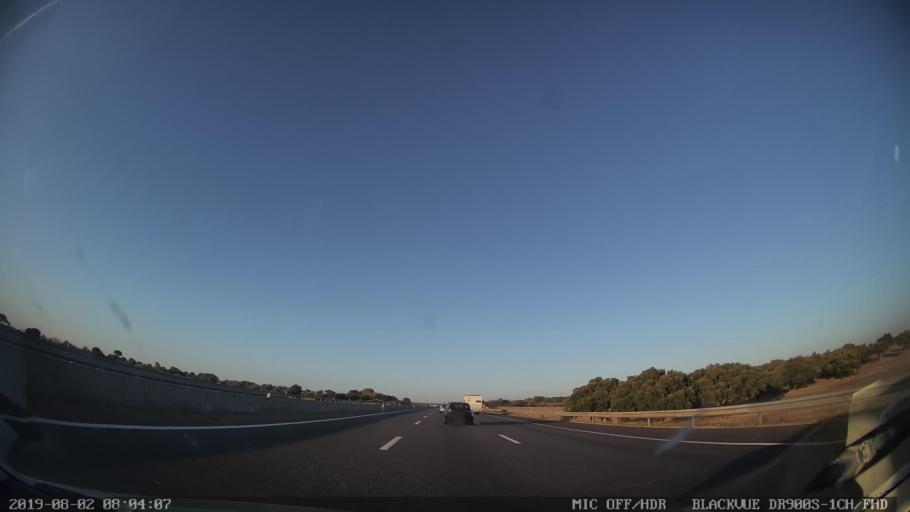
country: PT
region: Santarem
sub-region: Cartaxo
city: Pontevel
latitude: 39.1718
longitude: -8.8442
